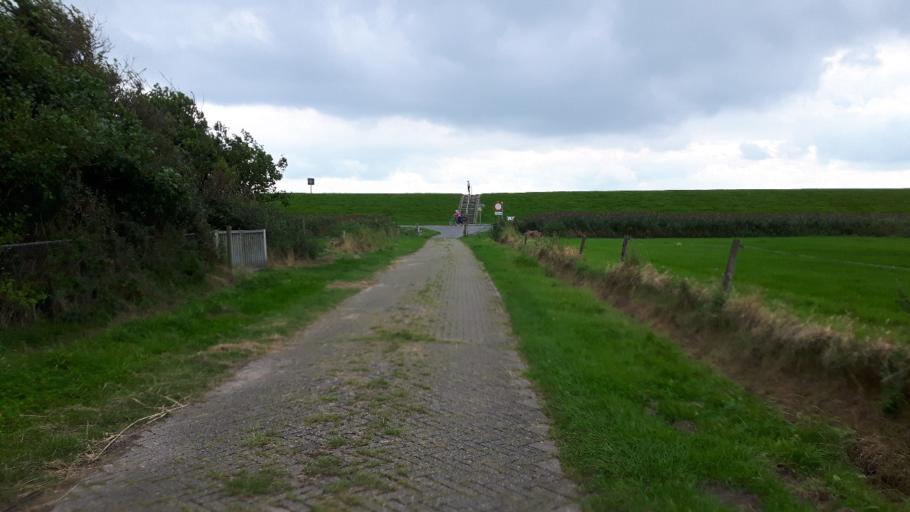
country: NL
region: Friesland
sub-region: Gemeente Ameland
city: Nes
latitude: 53.4433
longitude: 5.8300
